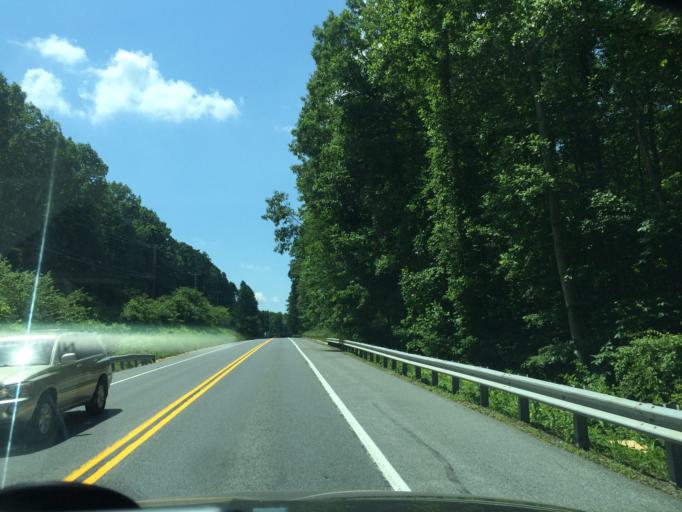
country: US
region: Maryland
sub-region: Carroll County
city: Eldersburg
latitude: 39.4304
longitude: -76.9363
